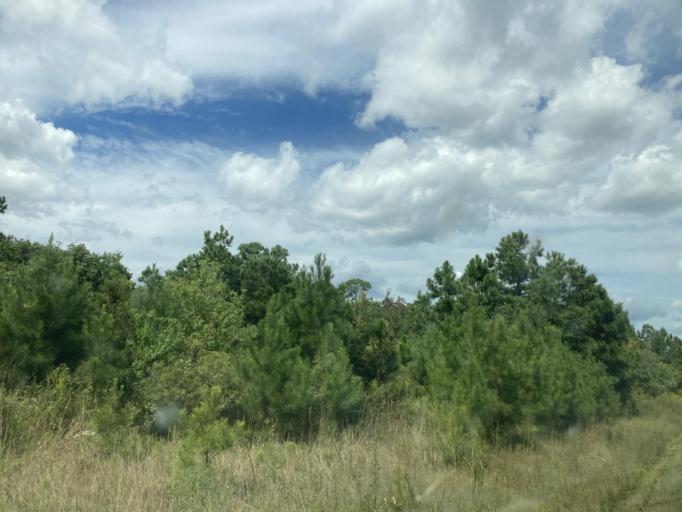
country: US
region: Mississippi
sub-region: Harrison County
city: D'Iberville
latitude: 30.4271
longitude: -88.8782
